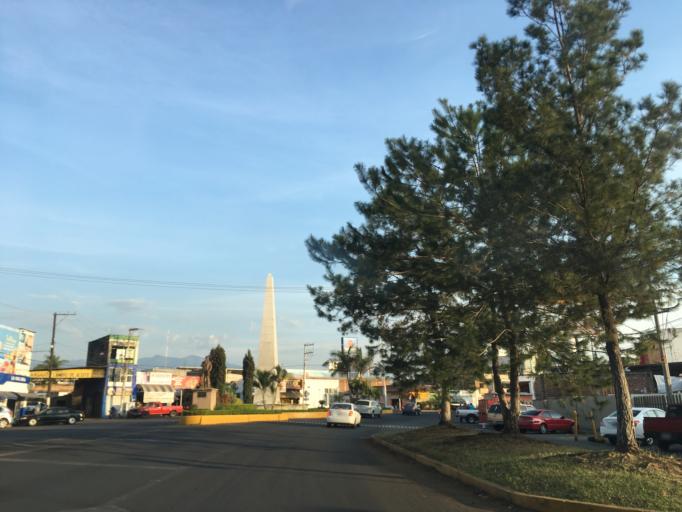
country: MX
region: Michoacan
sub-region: Los Reyes
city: La Higuerita (Colonia San Rafael)
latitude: 19.5949
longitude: -102.4729
